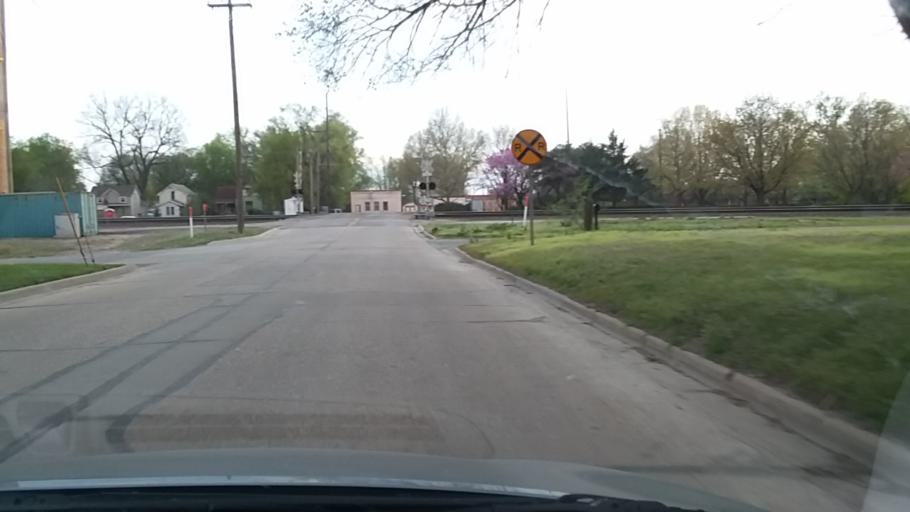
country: US
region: Kansas
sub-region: Douglas County
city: Lawrence
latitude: 38.9790
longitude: -95.2332
